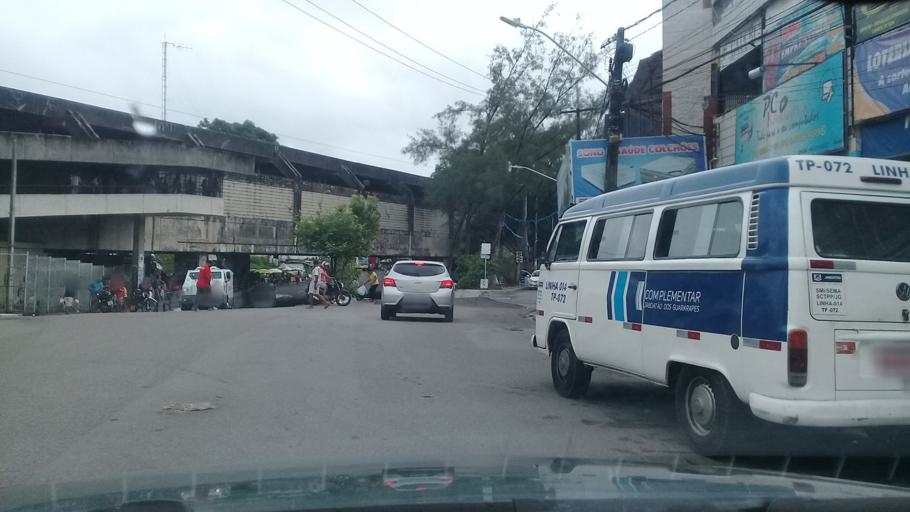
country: BR
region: Pernambuco
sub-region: Jaboatao Dos Guararapes
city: Jaboatao dos Guararapes
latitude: -8.0946
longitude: -34.9728
